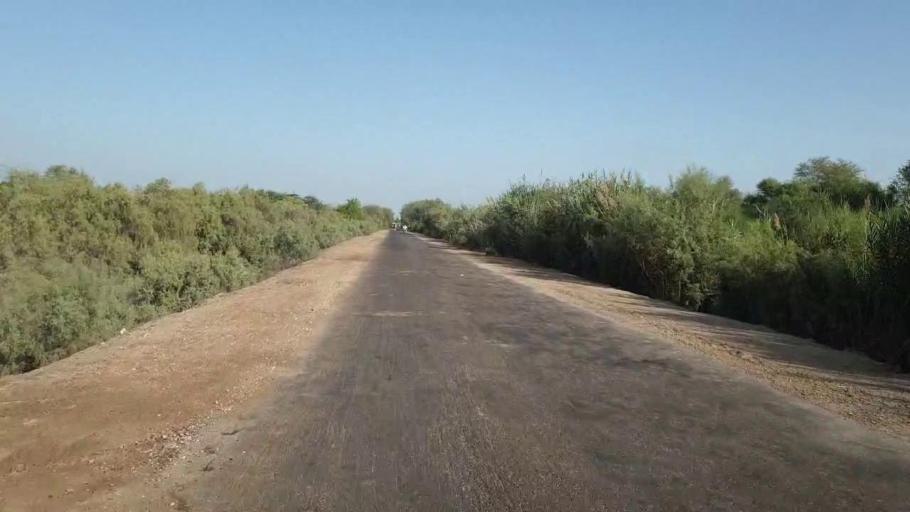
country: PK
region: Sindh
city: Nawabshah
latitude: 26.3822
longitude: 68.4570
